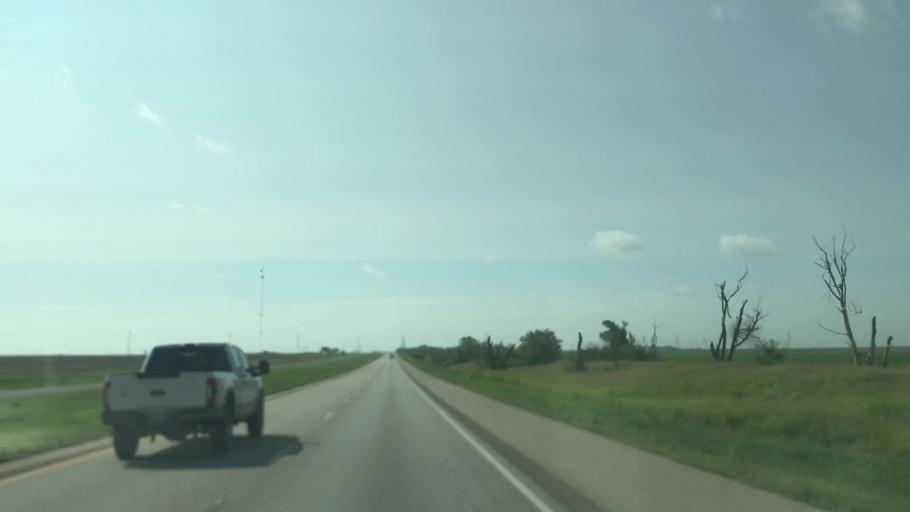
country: US
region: Texas
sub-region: Nolan County
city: Roscoe
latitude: 32.5699
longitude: -100.7154
